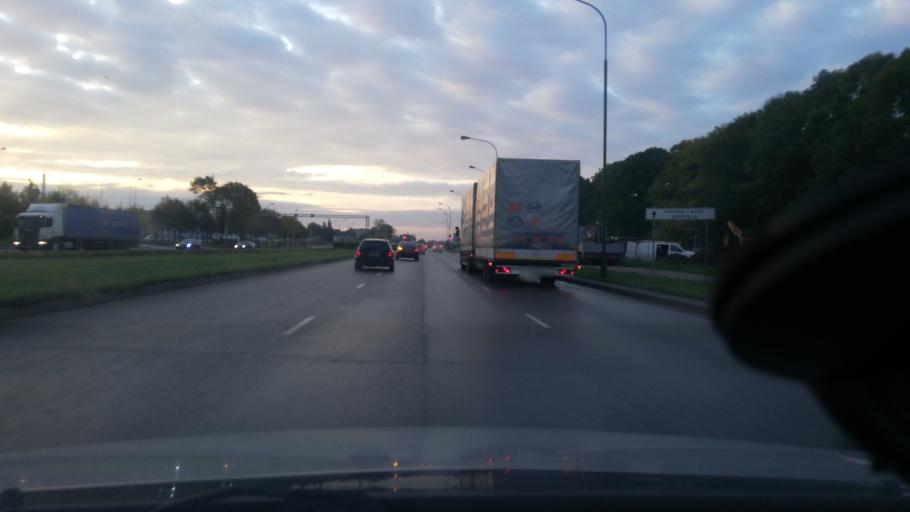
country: LT
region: Klaipedos apskritis
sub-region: Klaipeda
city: Klaipeda
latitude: 55.6916
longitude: 21.1785
